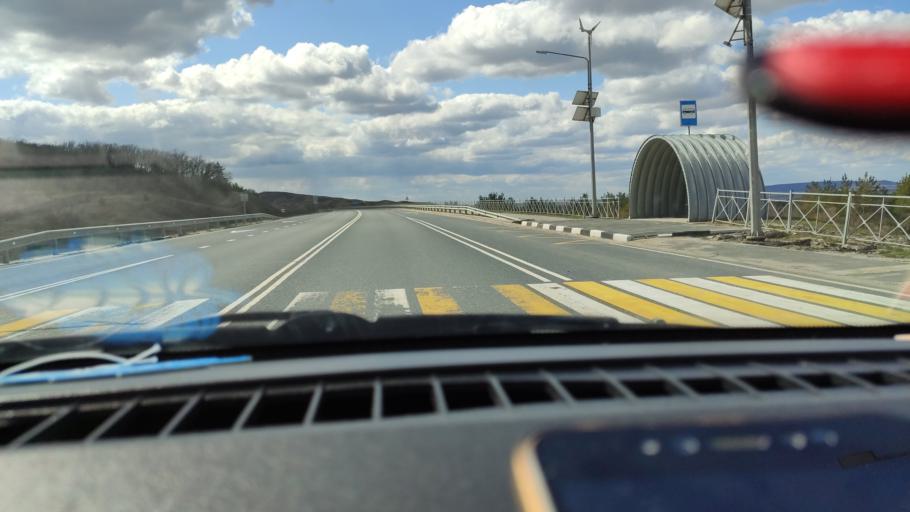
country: RU
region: Saratov
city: Alekseyevka
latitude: 52.3856
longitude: 47.9742
